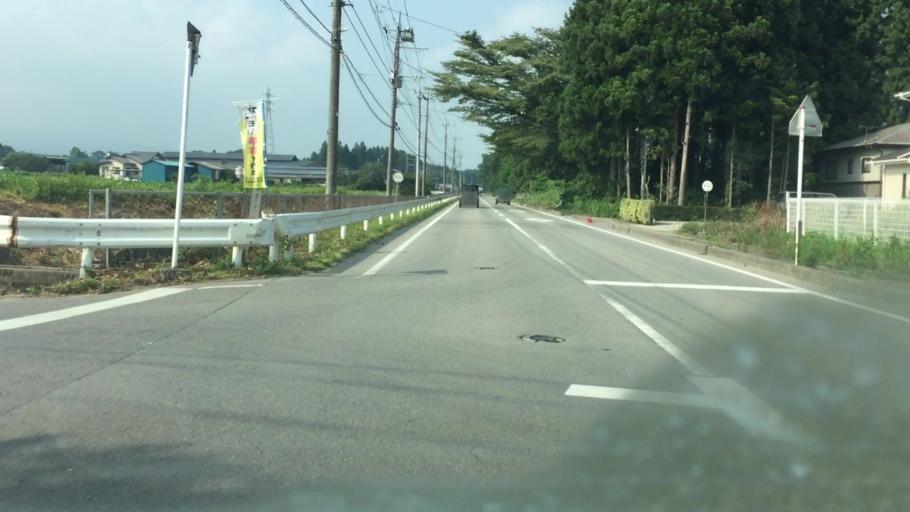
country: JP
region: Tochigi
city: Kuroiso
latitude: 37.0080
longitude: 140.0000
